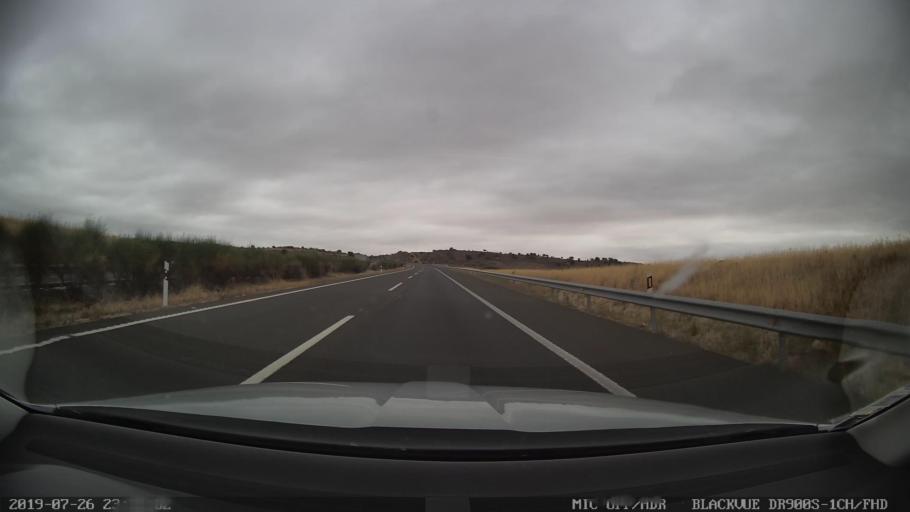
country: ES
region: Extremadura
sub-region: Provincia de Caceres
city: Trujillo
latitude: 39.4229
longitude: -5.8812
